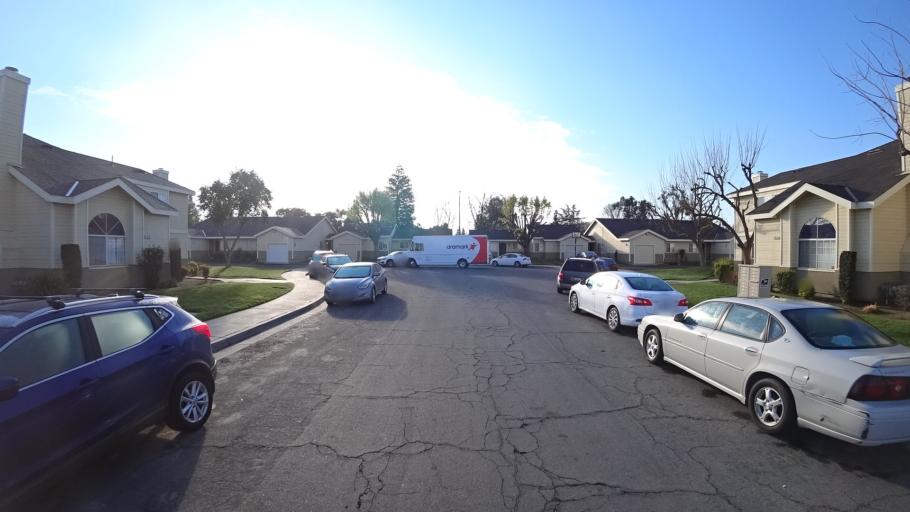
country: US
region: California
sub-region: Fresno County
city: West Park
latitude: 36.8172
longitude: -119.8718
